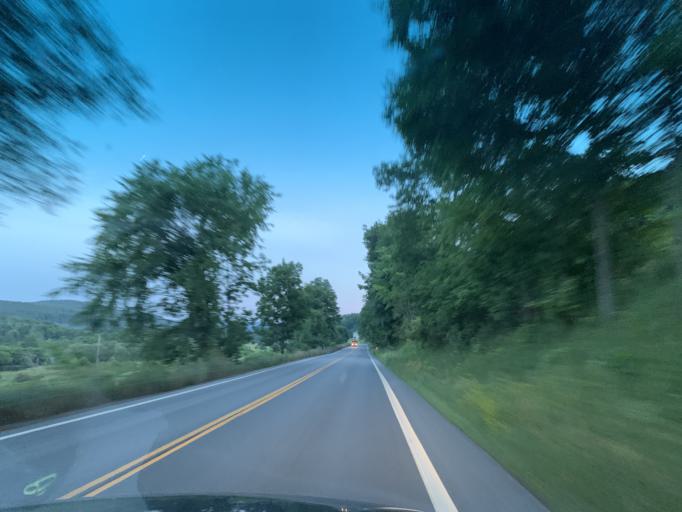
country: US
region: New York
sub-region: Chenango County
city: New Berlin
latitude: 42.6713
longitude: -75.3325
